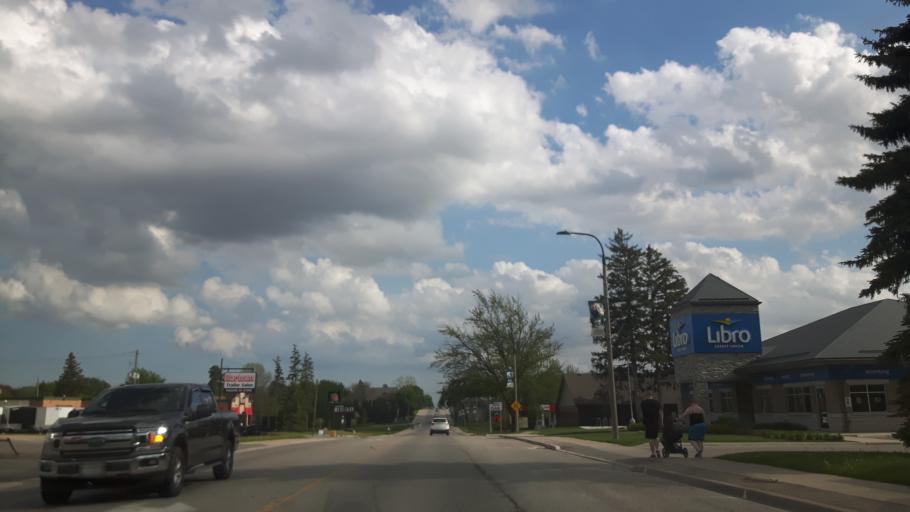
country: CA
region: Ontario
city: South Huron
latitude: 43.3592
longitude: -81.4830
